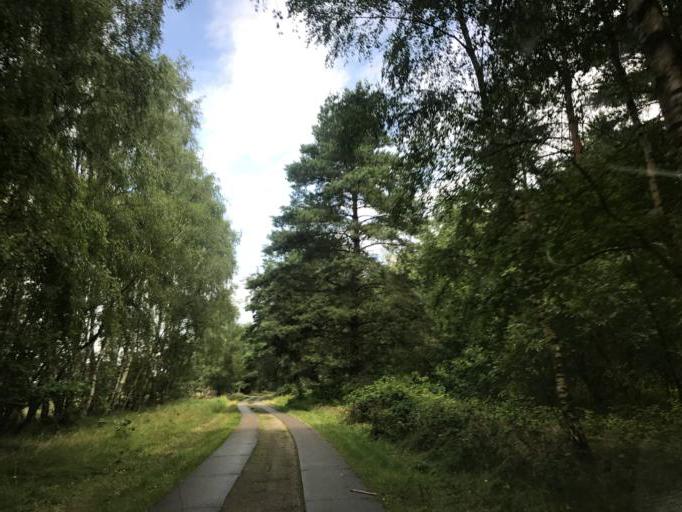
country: DE
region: Mecklenburg-Vorpommern
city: Wesenberg
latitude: 53.3756
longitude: 12.8939
